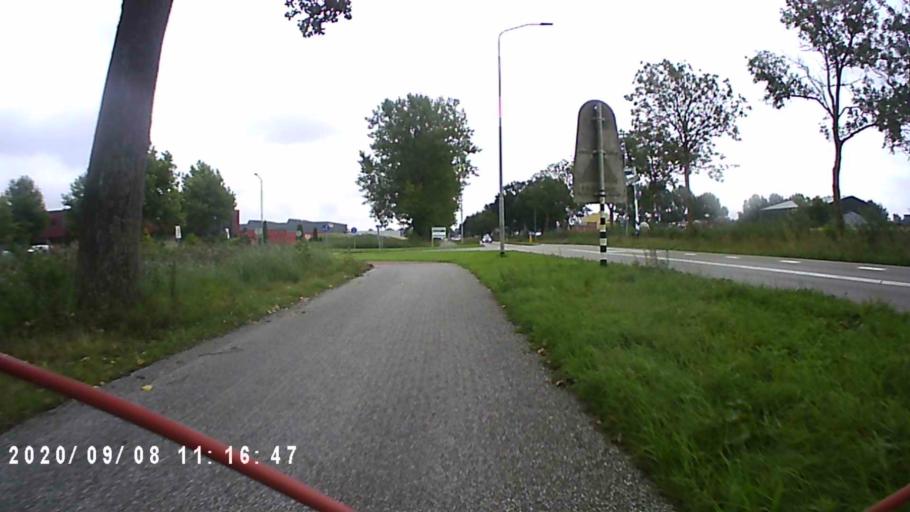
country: NL
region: Groningen
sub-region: Gemeente Hoogezand-Sappemeer
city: Hoogezand
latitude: 53.1710
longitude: 6.7329
